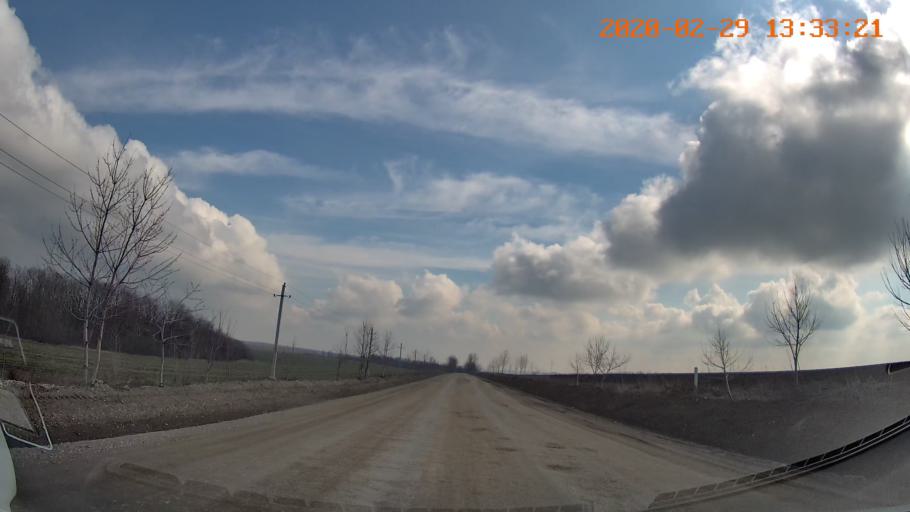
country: MD
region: Telenesti
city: Camenca
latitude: 47.8740
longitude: 28.6159
